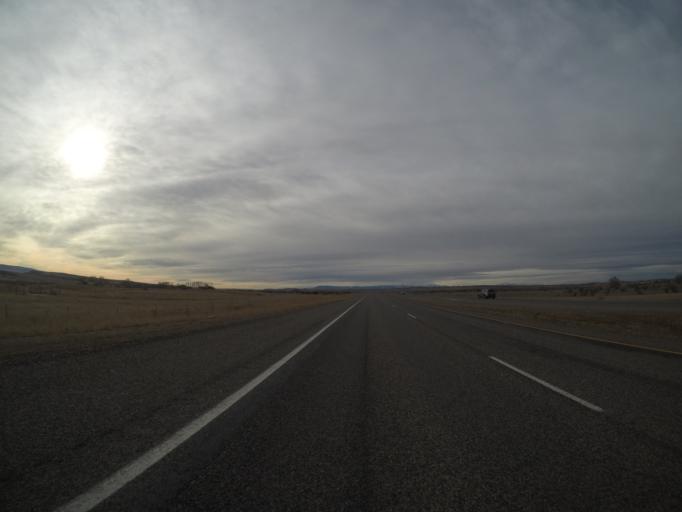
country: US
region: Montana
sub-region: Yellowstone County
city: Laurel
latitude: 45.5965
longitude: -108.8264
